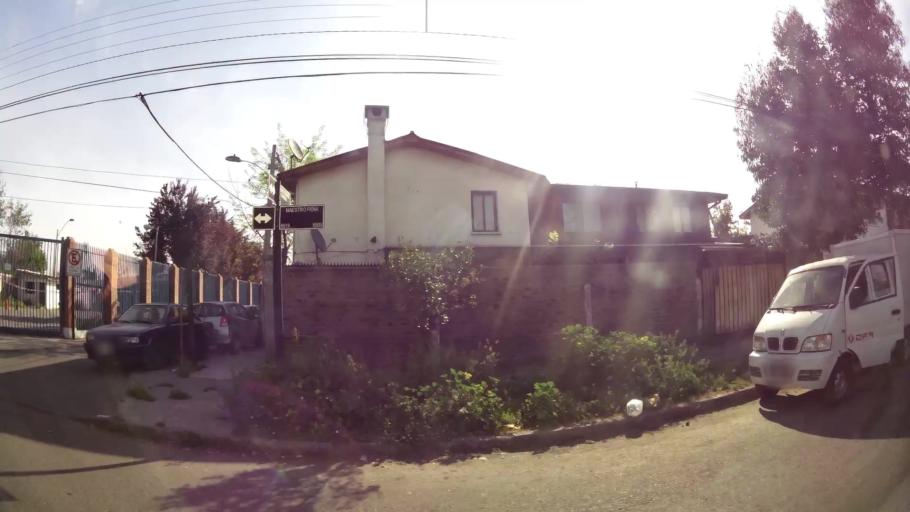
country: CL
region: Santiago Metropolitan
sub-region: Provincia de Santiago
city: La Pintana
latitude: -33.5217
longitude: -70.6345
